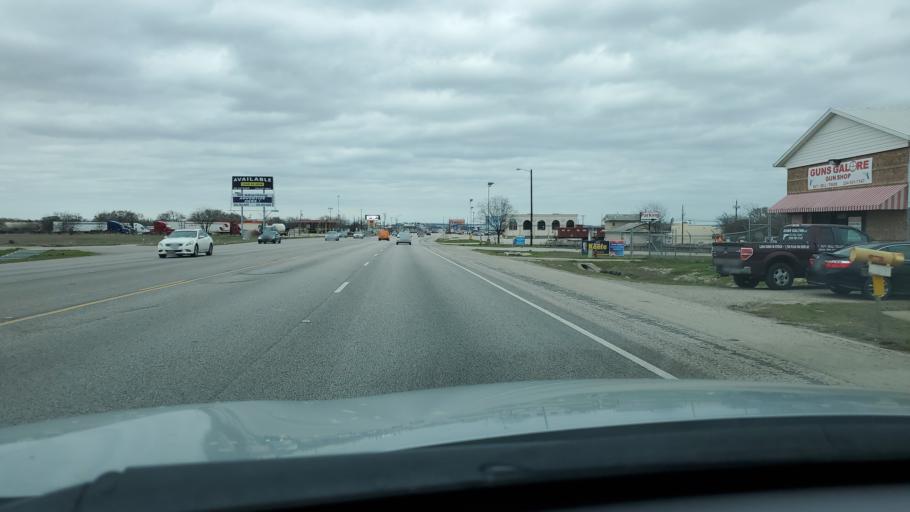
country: US
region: Texas
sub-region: Bell County
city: Killeen
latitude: 31.0826
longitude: -97.7566
